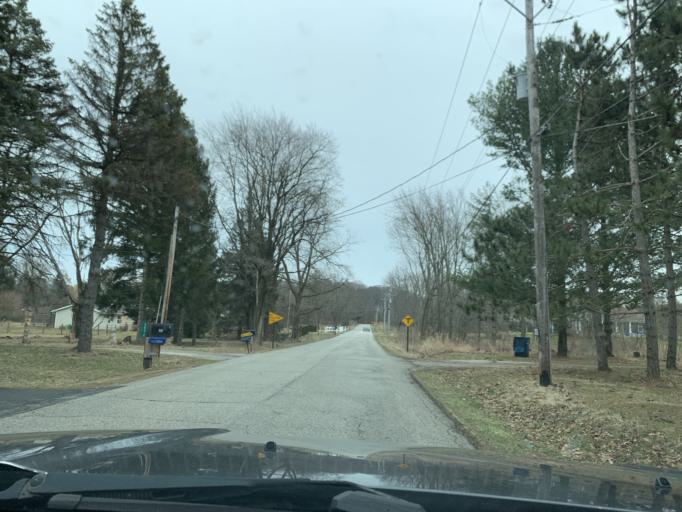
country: US
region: Indiana
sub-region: Porter County
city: Chesterton
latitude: 41.5856
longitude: -86.9940
